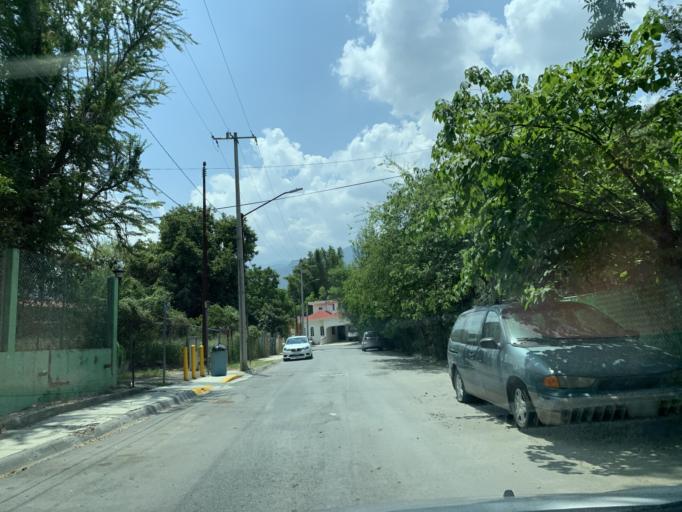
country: MX
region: Nuevo Leon
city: Santiago
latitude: 25.4016
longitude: -100.1301
